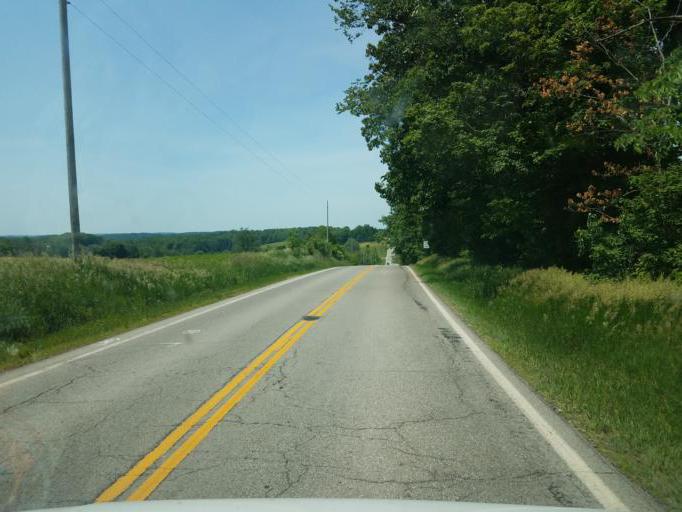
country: US
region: Ohio
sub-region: Ashland County
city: Loudonville
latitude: 40.7169
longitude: -82.2249
